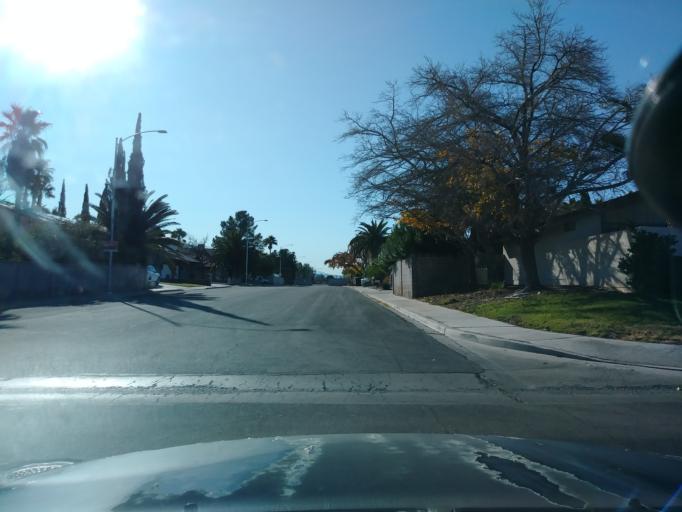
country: US
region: Nevada
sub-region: Clark County
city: Spring Valley
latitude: 36.1479
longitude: -115.2298
